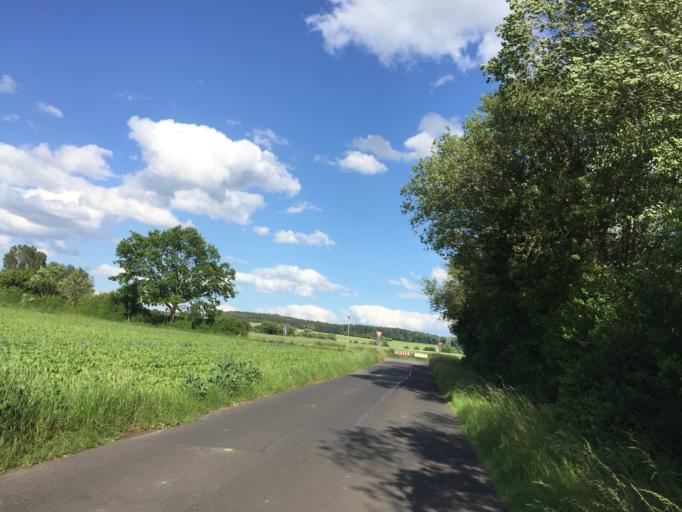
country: DE
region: Hesse
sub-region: Regierungsbezirk Darmstadt
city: Karben
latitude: 50.2469
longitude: 8.7735
